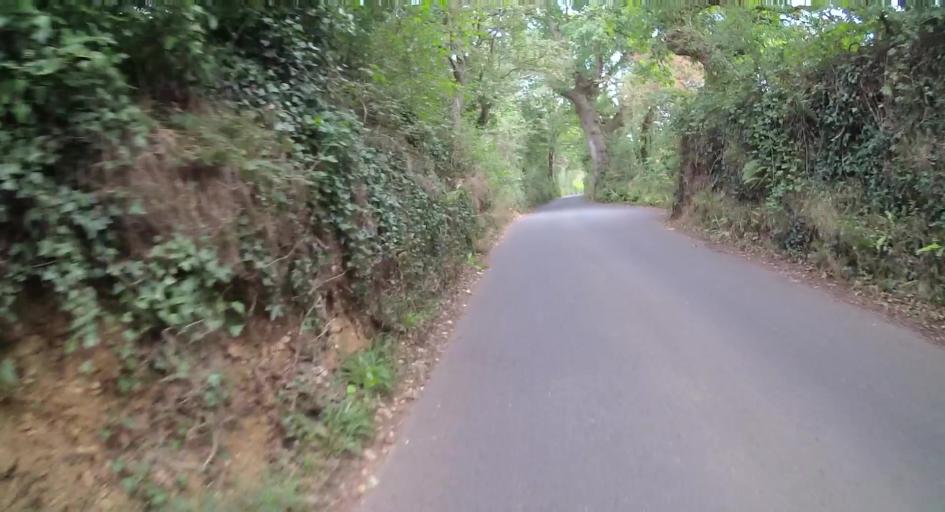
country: GB
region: England
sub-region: Isle of Wight
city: Niton
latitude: 50.6293
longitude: -1.2702
